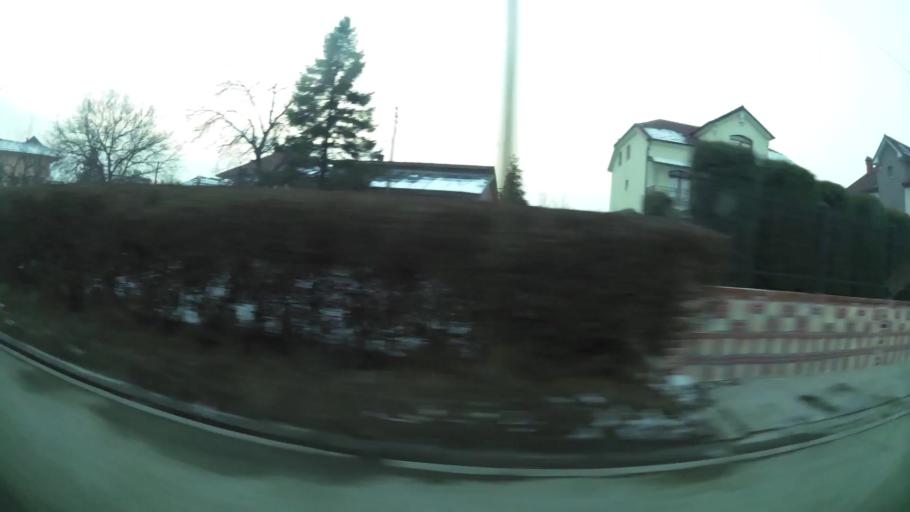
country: MK
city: Creshevo
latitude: 42.0062
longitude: 21.5176
